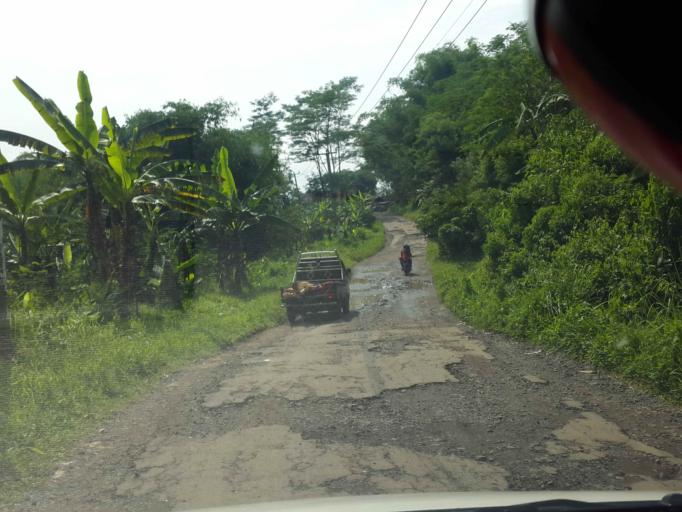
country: ID
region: West Java
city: Pasirreungit
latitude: -6.9308
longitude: 107.0064
